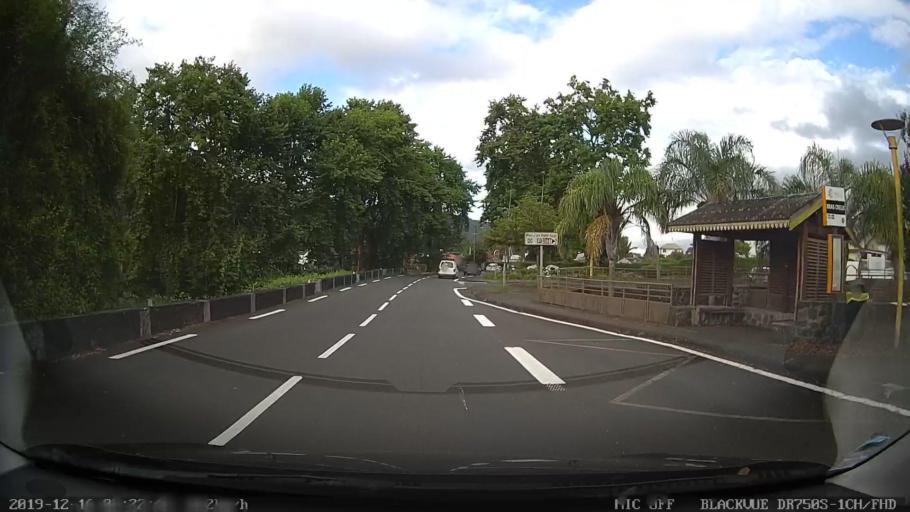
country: RE
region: Reunion
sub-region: Reunion
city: Salazie
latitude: -21.1462
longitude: 55.6180
